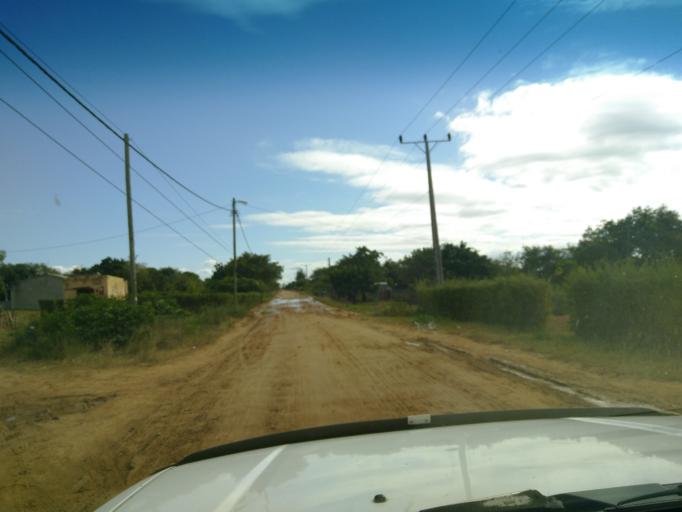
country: MZ
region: Maputo City
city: Maputo
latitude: -26.0005
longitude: 32.5425
